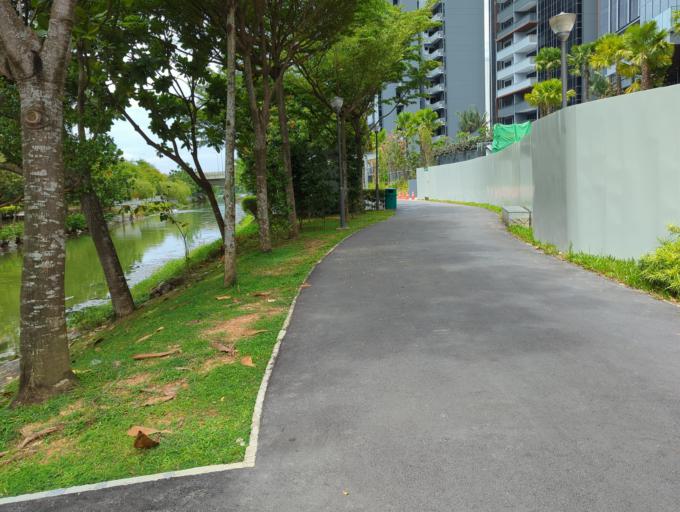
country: MY
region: Johor
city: Kampung Pasir Gudang Baru
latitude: 1.4095
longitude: 103.8985
